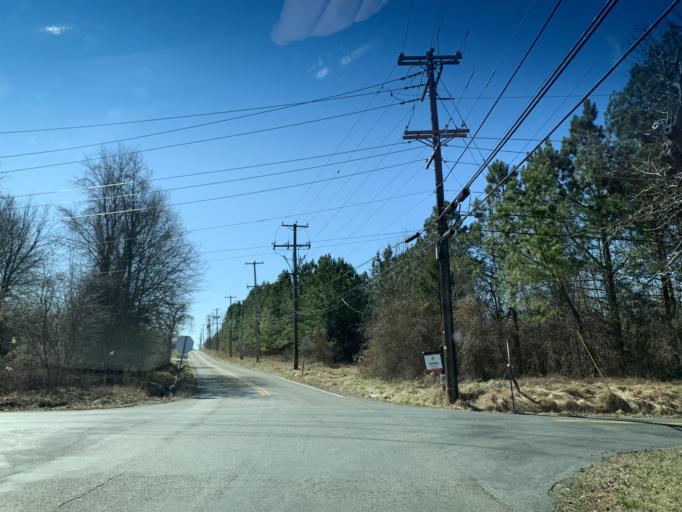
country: US
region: Maryland
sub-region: Cecil County
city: Elkton
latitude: 39.5157
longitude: -75.8258
